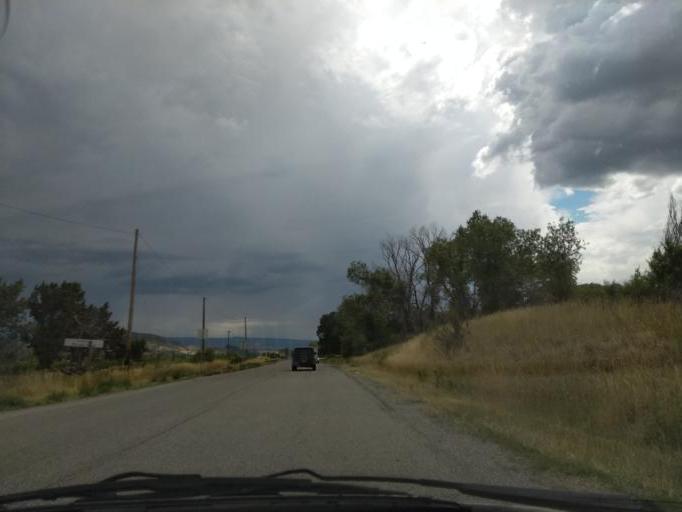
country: US
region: Colorado
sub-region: Delta County
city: Paonia
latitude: 38.8874
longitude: -107.5861
